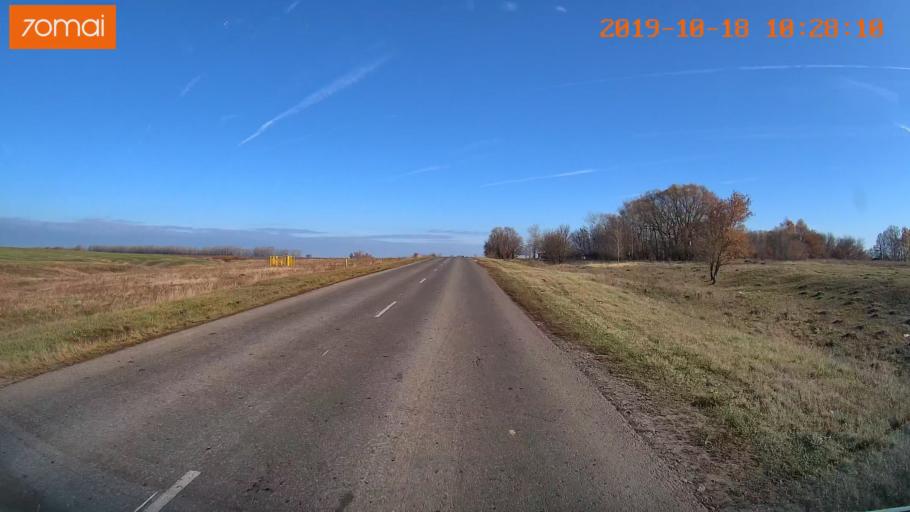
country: RU
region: Tula
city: Kurkino
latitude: 53.4412
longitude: 38.6506
